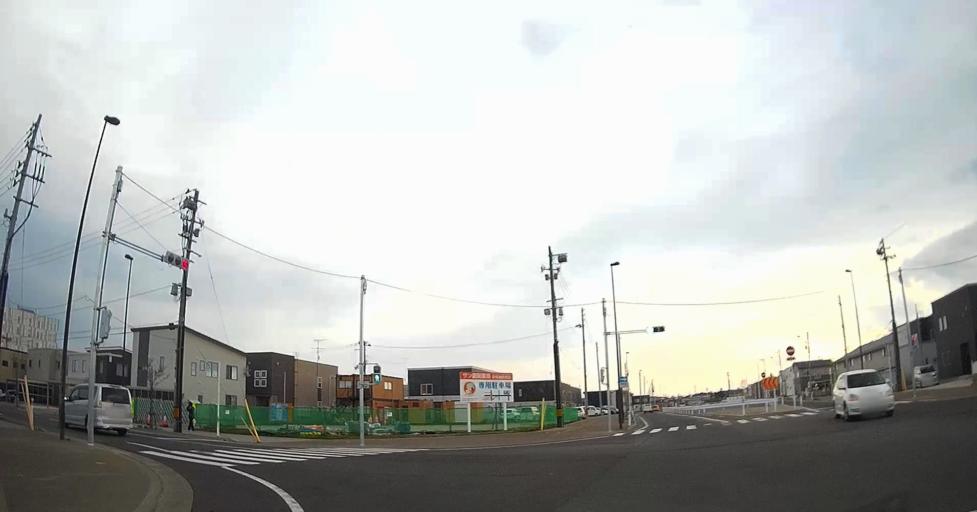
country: JP
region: Aomori
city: Aomori Shi
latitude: 40.8309
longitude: 140.6902
